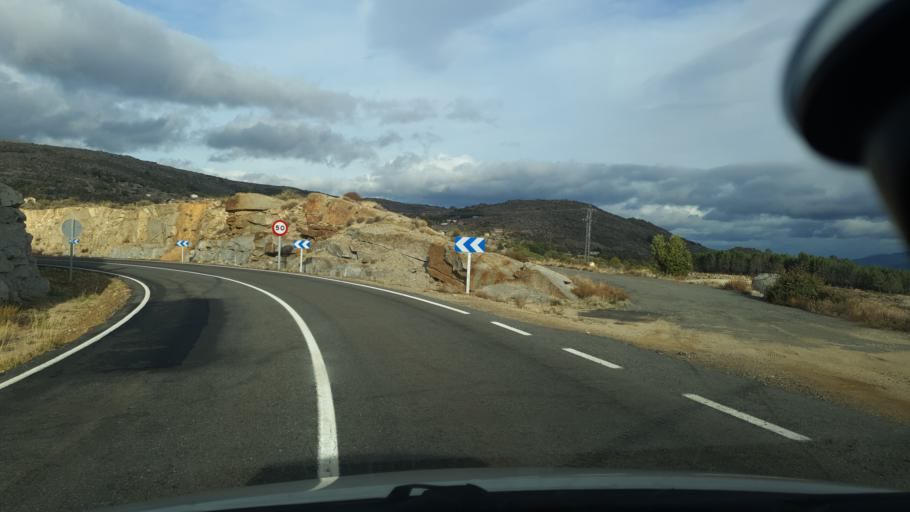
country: ES
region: Castille and Leon
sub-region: Provincia de Avila
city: Navalosa
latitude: 40.3926
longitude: -4.9425
